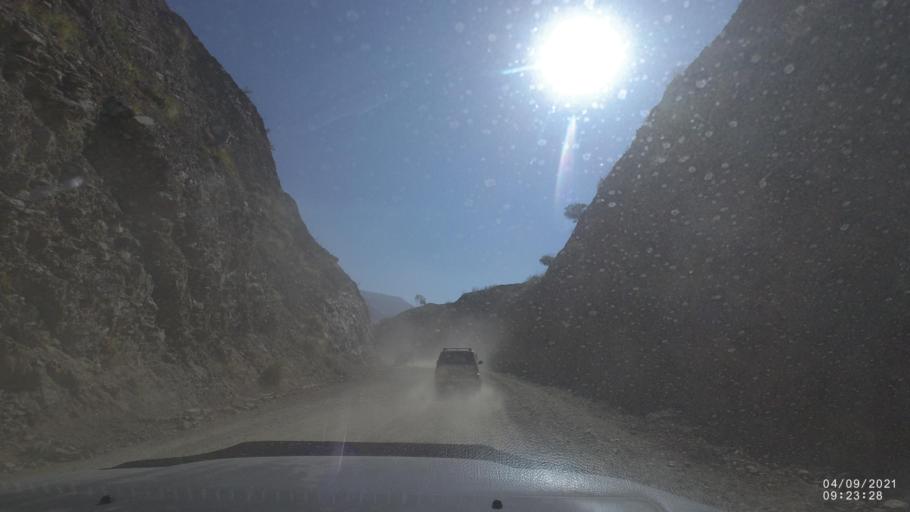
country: BO
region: Cochabamba
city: Sipe Sipe
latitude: -17.3635
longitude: -66.3675
